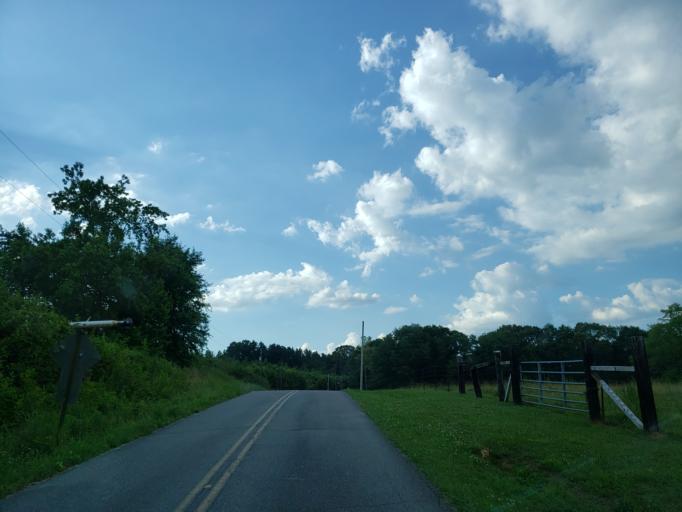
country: US
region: Georgia
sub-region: Polk County
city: Cedartown
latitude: 33.9205
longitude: -85.2699
